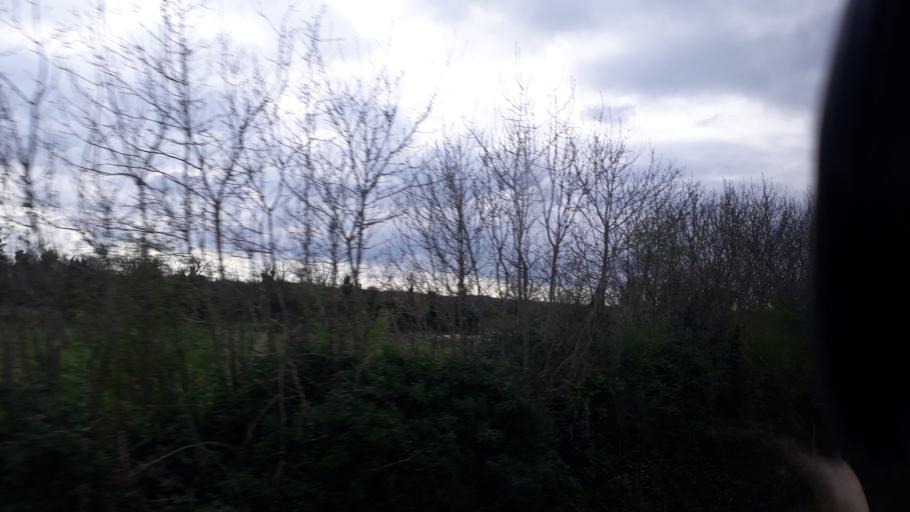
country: IE
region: Leinster
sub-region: An Longfort
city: Longford
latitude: 53.7074
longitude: -7.7202
